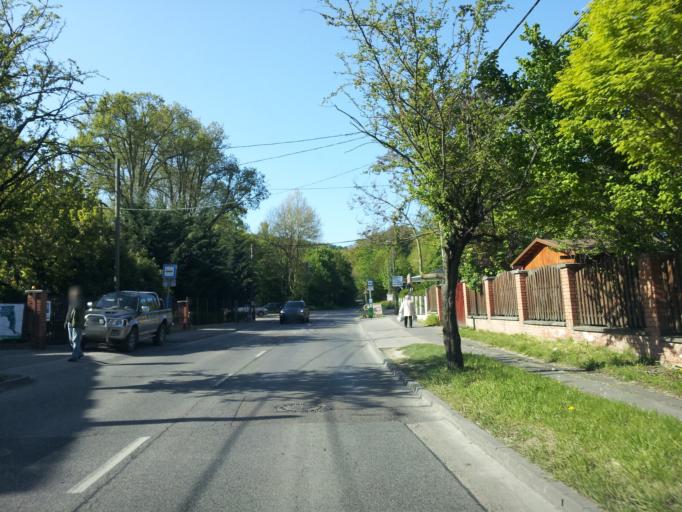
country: HU
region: Pest
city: Budakeszi
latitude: 47.5456
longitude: 18.9528
